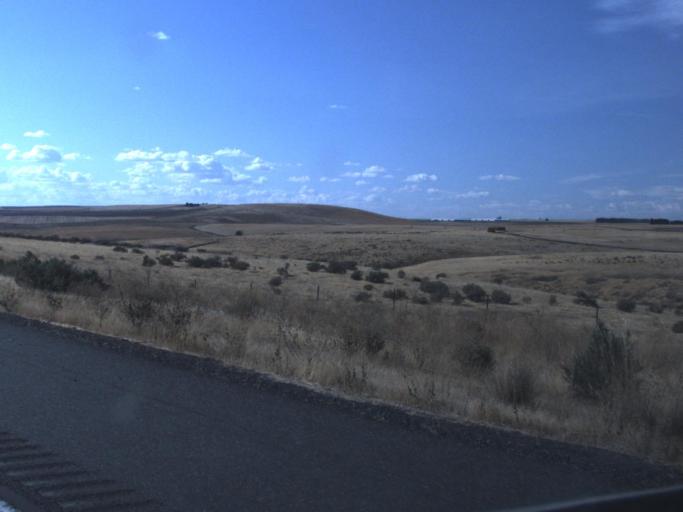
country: US
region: Oregon
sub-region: Umatilla County
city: Umatilla
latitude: 45.9914
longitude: -119.2922
